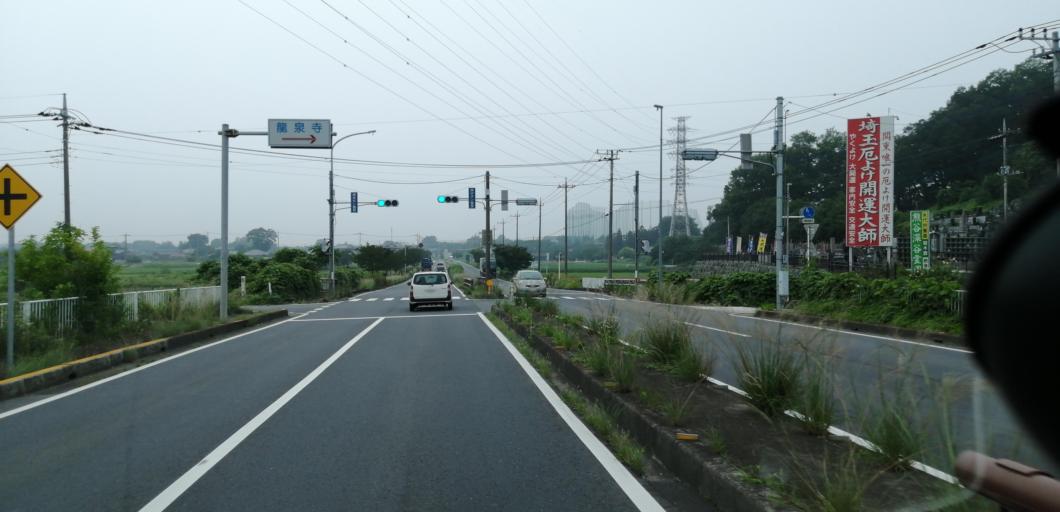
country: JP
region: Saitama
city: Fukayacho
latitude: 36.1510
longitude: 139.3143
